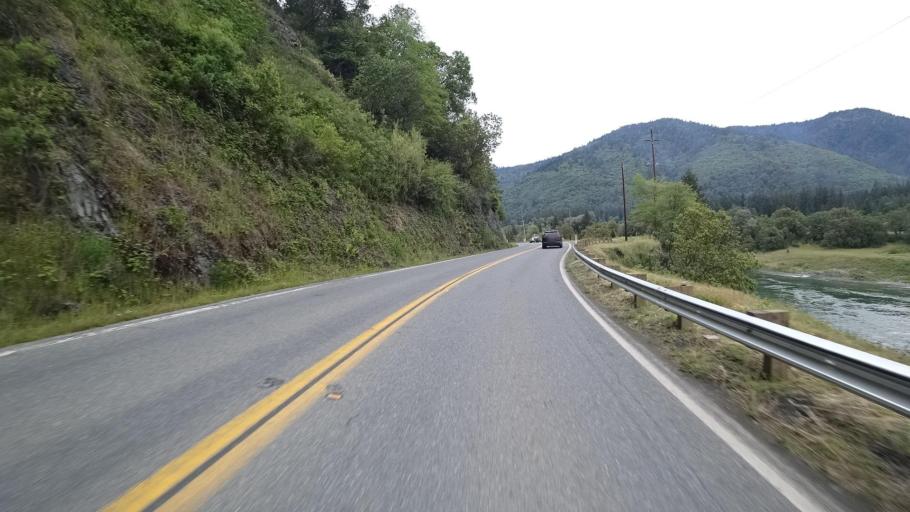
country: US
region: California
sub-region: Humboldt County
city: Willow Creek
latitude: 41.0394
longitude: -123.6717
